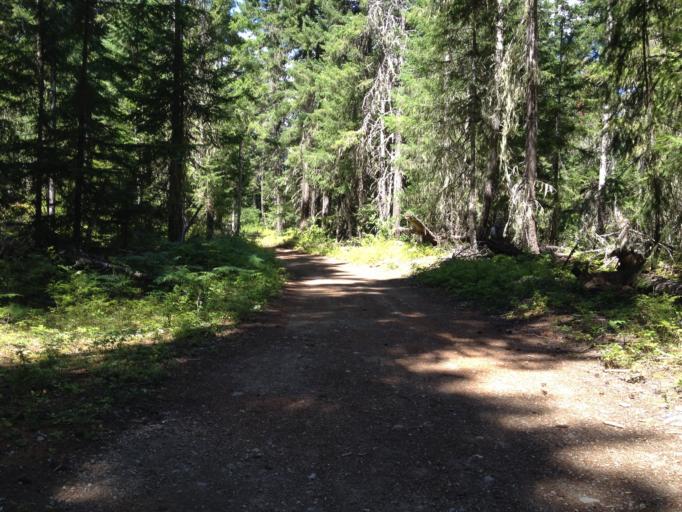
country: US
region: Washington
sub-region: Kittitas County
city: Cle Elum
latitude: 47.2548
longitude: -121.2080
